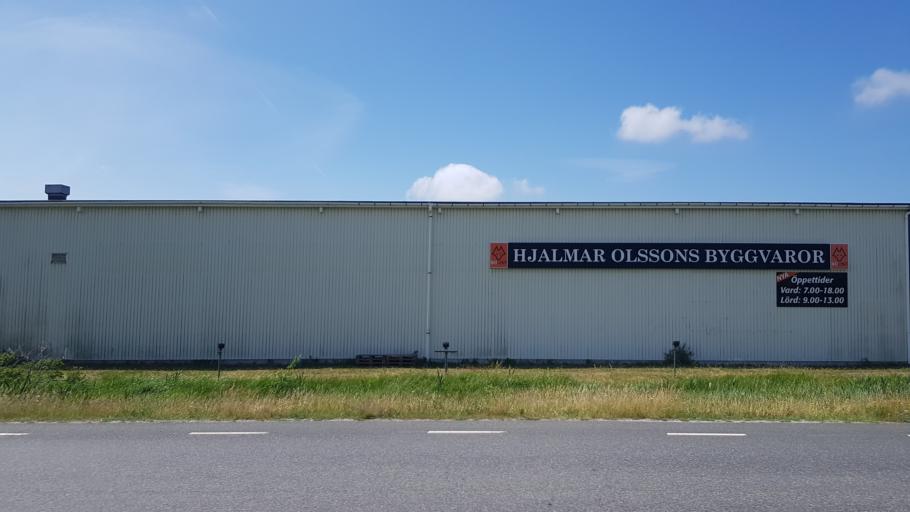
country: SE
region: Vaestra Goetaland
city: Ronnang
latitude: 57.9490
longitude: 11.5690
